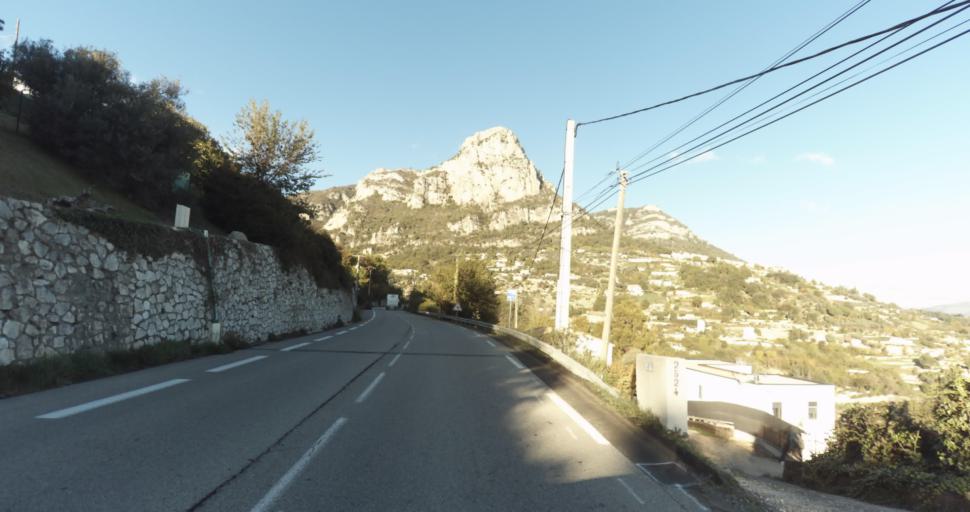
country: FR
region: Provence-Alpes-Cote d'Azur
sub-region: Departement des Alpes-Maritimes
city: Saint-Jeannet
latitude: 43.7407
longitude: 7.1320
